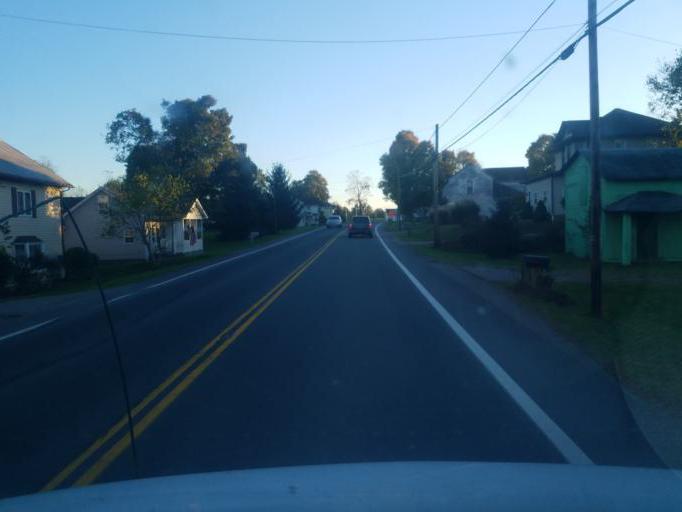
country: US
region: Ohio
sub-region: Licking County
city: Newark
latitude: 40.1278
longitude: -82.4290
